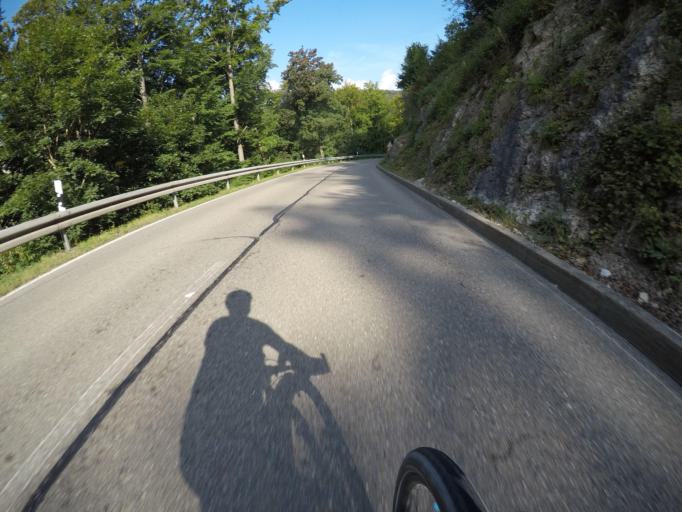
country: DE
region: Baden-Wuerttemberg
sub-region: Regierungsbezirk Stuttgart
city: Geislingen an der Steige
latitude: 48.6375
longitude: 9.8784
